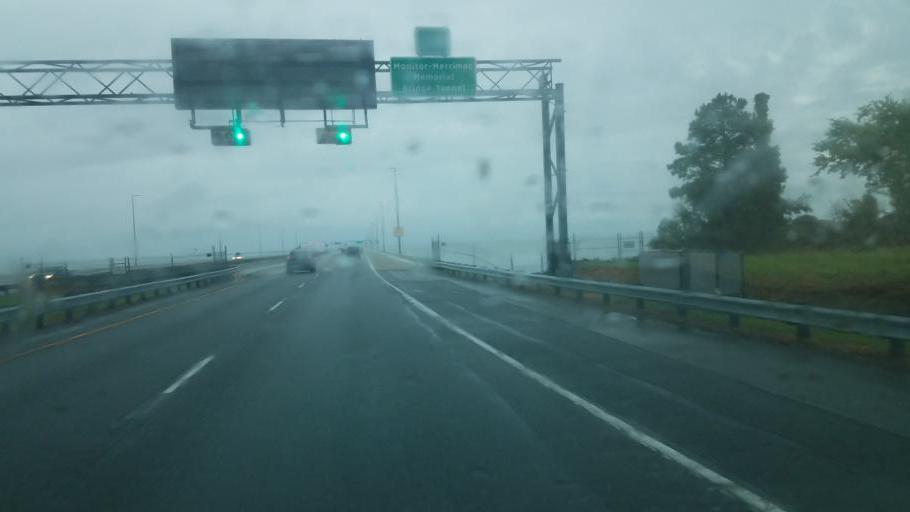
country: US
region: Virginia
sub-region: City of Newport News
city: Newport News
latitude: 36.9013
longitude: -76.4235
